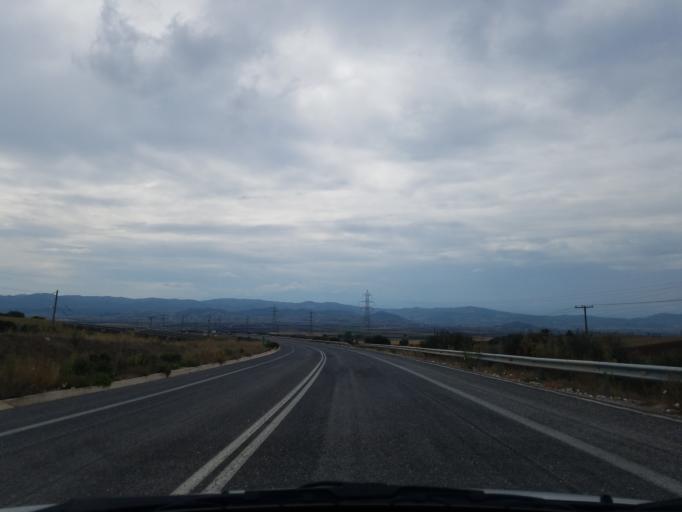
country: GR
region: Central Greece
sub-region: Nomos Fthiotidos
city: Domokos
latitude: 39.0962
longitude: 22.3047
